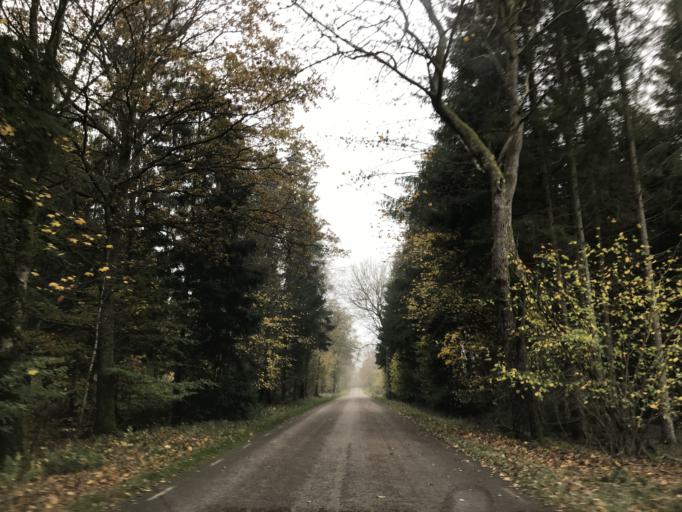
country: SE
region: Skane
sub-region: Svalovs Kommun
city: Kagerod
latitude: 55.9716
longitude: 13.0709
